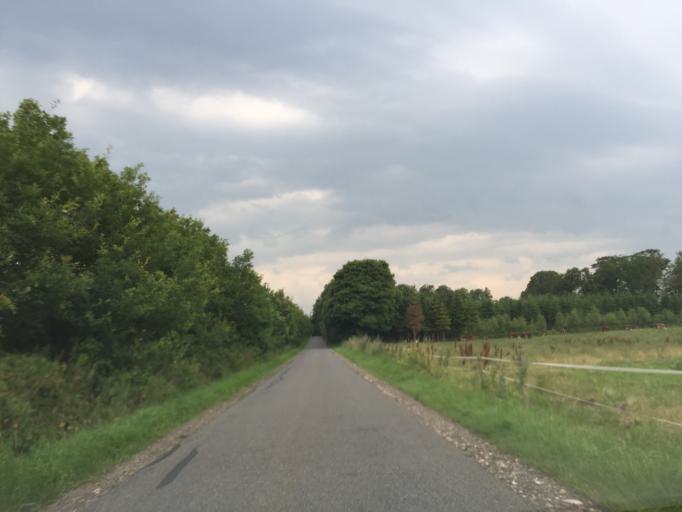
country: DK
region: Central Jutland
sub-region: Viborg Kommune
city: Bjerringbro
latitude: 56.3236
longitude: 9.6649
